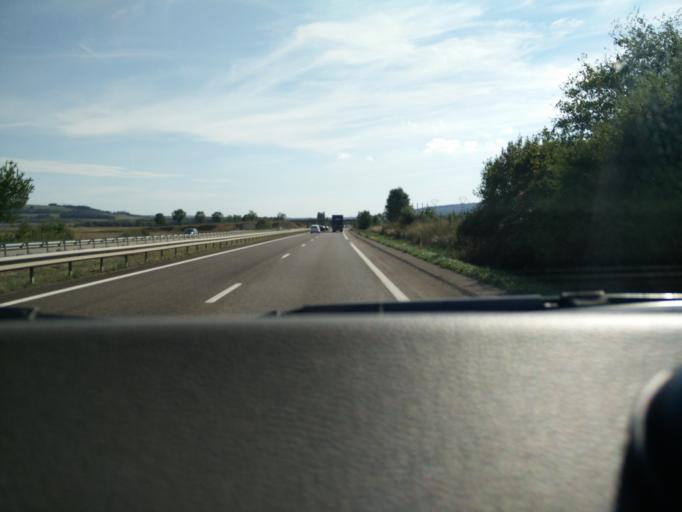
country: FR
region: Lorraine
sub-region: Departement de Meurthe-et-Moselle
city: Pont-a-Mousson
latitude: 48.8973
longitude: 6.1039
